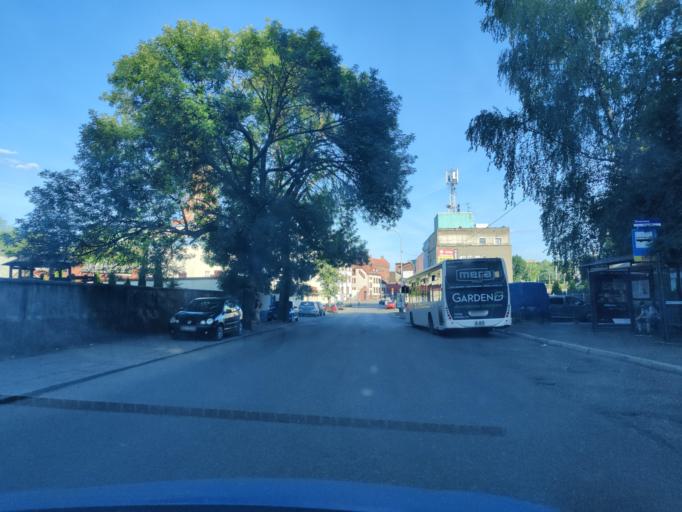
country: PL
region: Silesian Voivodeship
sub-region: Myslowice
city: Myslowice
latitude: 50.2434
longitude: 19.1369
